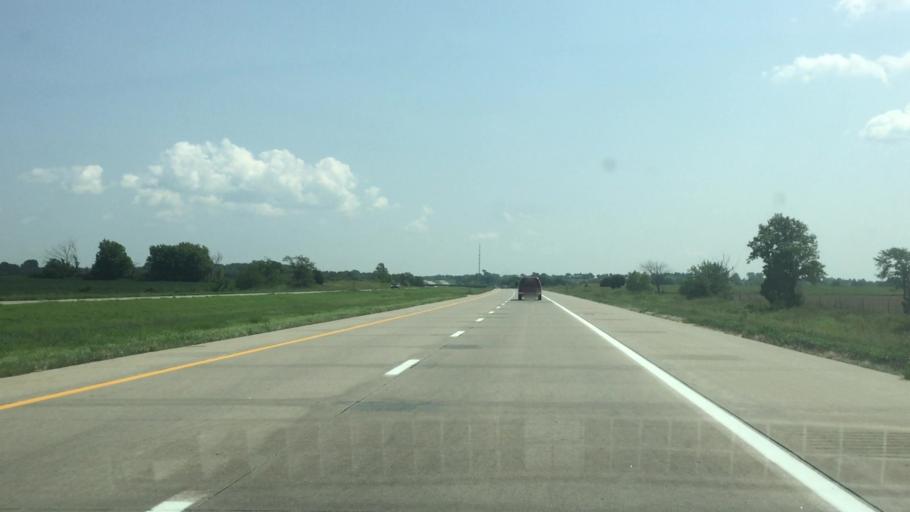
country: US
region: Kansas
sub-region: Franklin County
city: Ottawa
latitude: 38.5569
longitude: -95.3353
